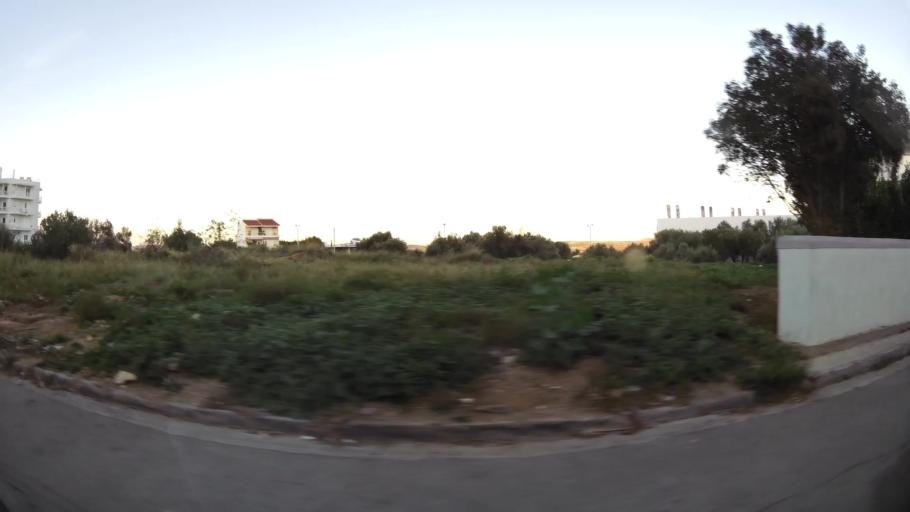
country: GR
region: Attica
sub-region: Nomarchia Anatolikis Attikis
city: Spata
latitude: 37.9624
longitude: 23.9252
